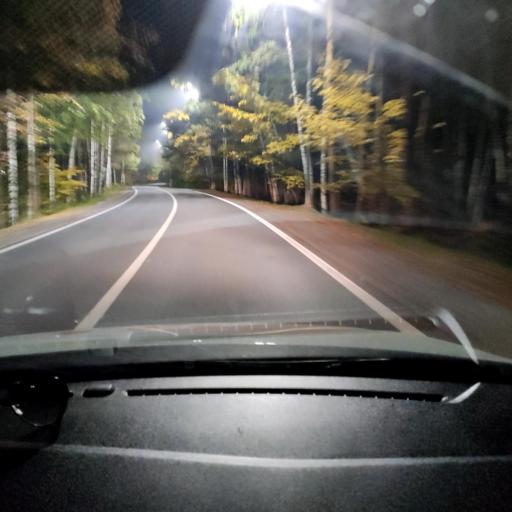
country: RU
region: Tatarstan
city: Verkhniy Uslon
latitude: 55.6328
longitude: 49.0181
